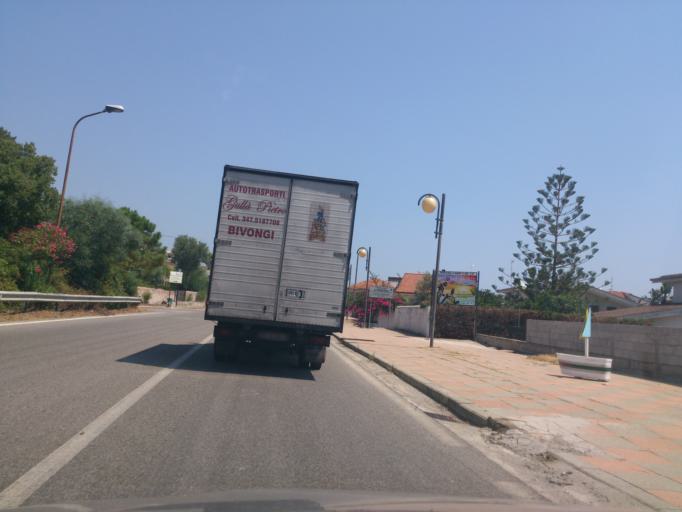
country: IT
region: Calabria
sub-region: Provincia di Reggio Calabria
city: Riace Marina
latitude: 38.3877
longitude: 16.5271
